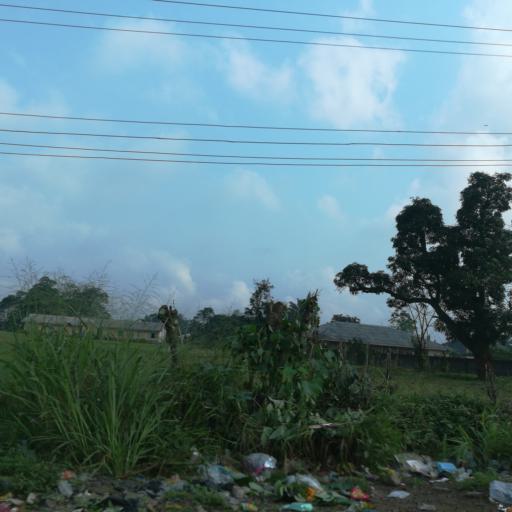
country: NG
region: Rivers
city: Okrika
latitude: 4.7816
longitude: 7.1493
